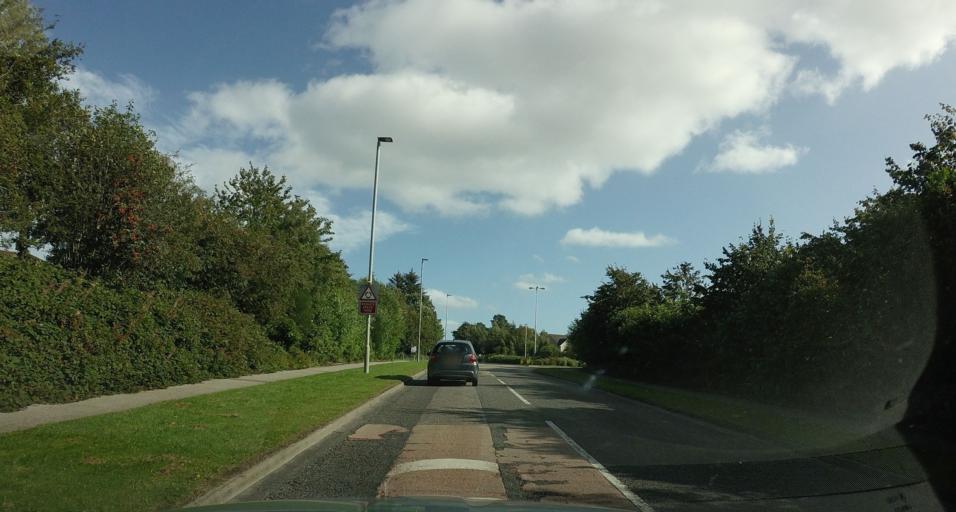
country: GB
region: Scotland
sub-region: Aberdeenshire
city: Westhill
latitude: 57.1513
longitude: -2.3037
